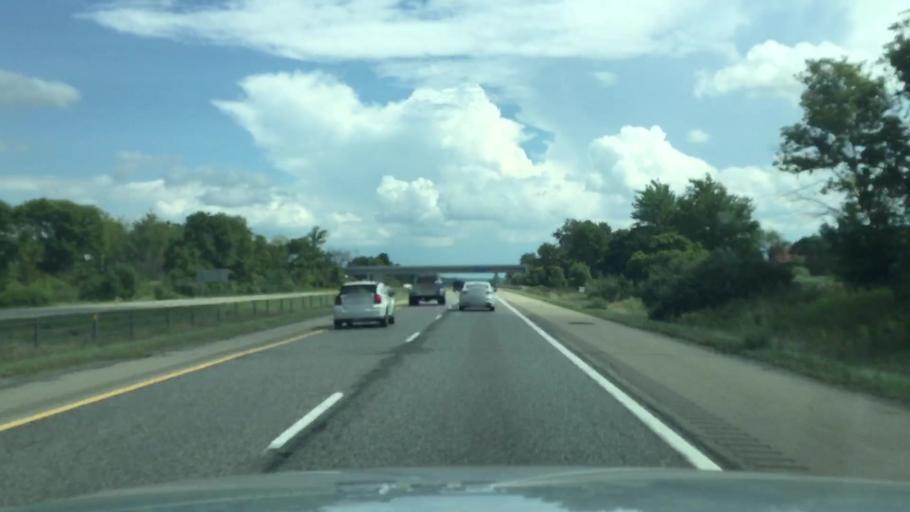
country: US
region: Michigan
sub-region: Washtenaw County
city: Chelsea
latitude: 42.2955
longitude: -84.0092
